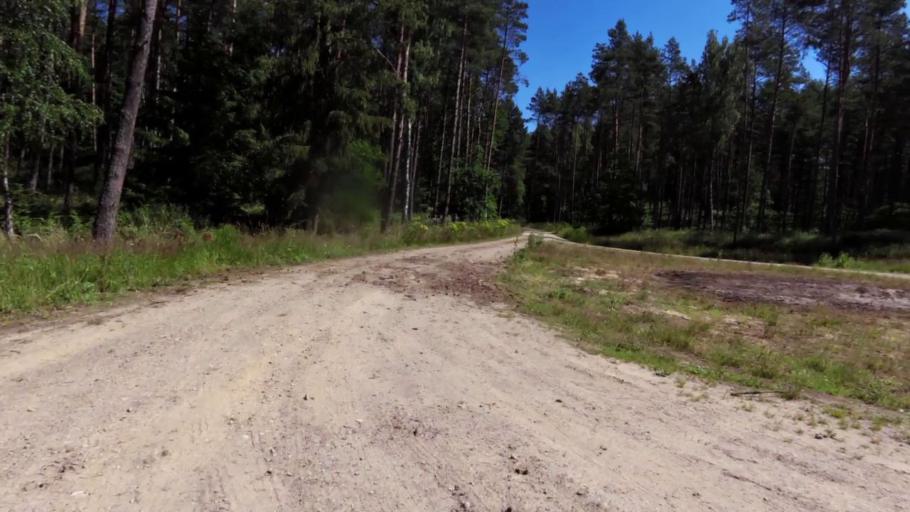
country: PL
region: West Pomeranian Voivodeship
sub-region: Powiat swidwinski
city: Rabino
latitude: 53.8587
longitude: 16.0313
